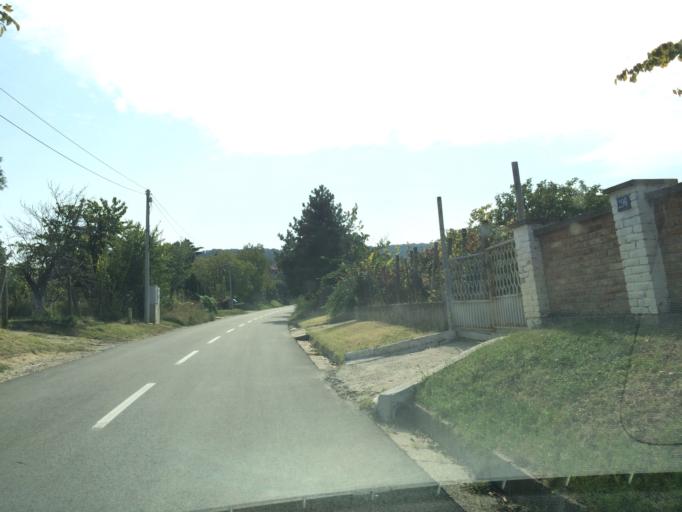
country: RS
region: Autonomna Pokrajina Vojvodina
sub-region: Juznobacki Okrug
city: Novi Sad
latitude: 45.1908
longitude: 19.8342
